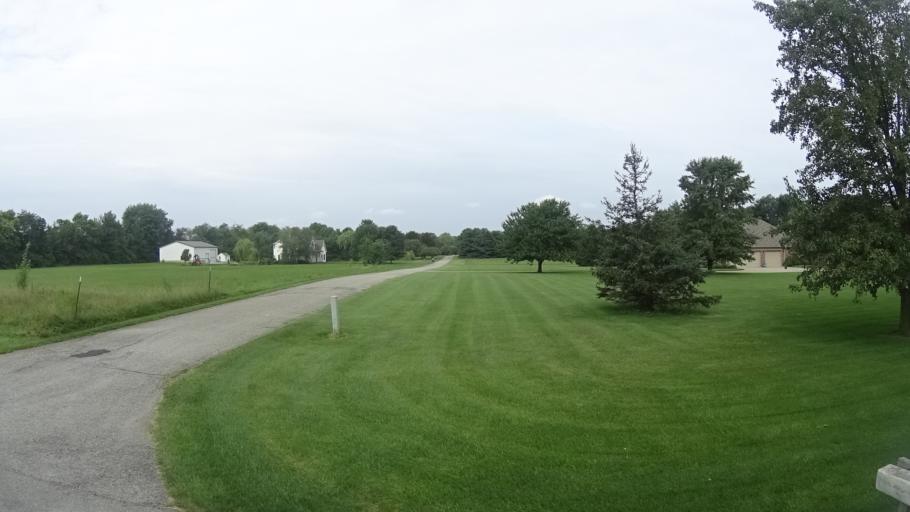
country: US
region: Indiana
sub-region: Madison County
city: Pendleton
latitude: 40.0070
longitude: -85.7870
